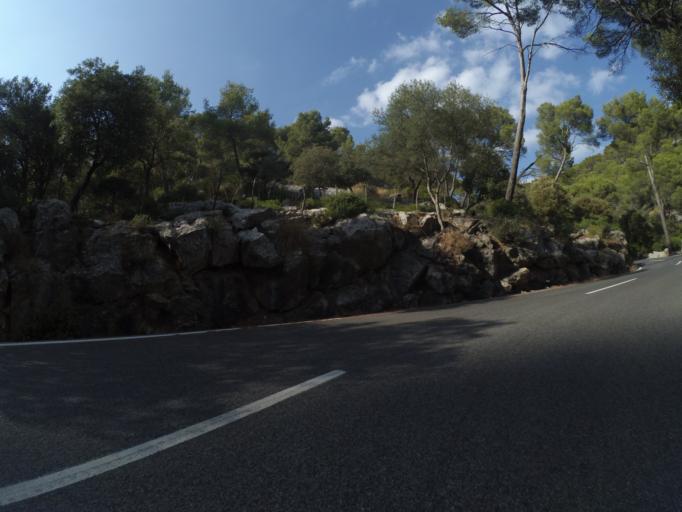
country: ES
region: Balearic Islands
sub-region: Illes Balears
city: Selva
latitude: 39.7901
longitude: 2.8903
